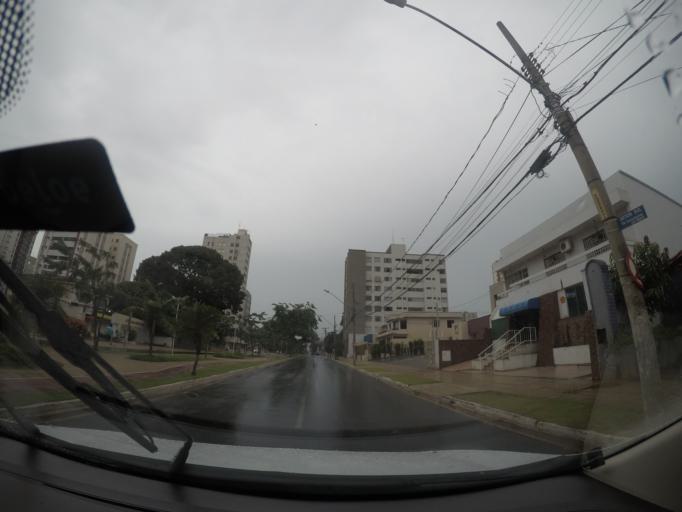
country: BR
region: Goias
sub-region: Goiania
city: Goiania
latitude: -16.6817
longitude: -49.2599
